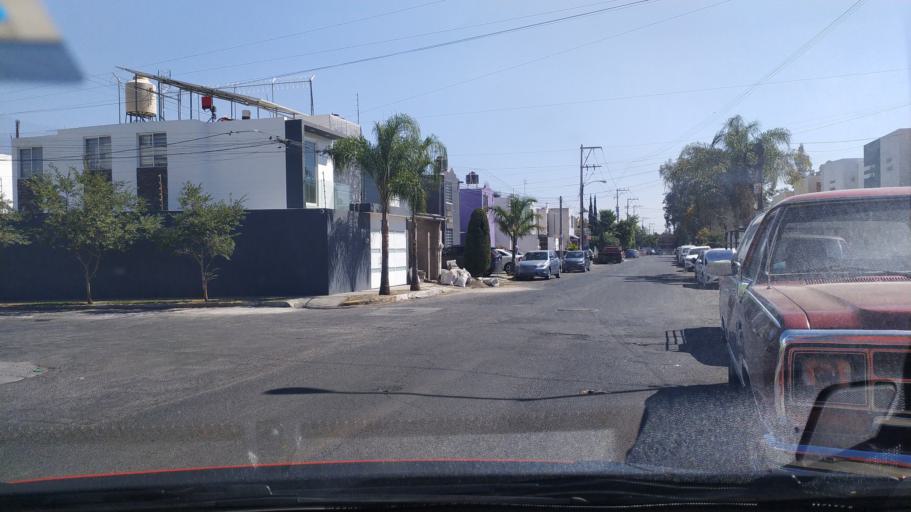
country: MX
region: Jalisco
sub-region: Tlajomulco de Zuniga
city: Palomar
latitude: 20.6290
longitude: -103.4633
